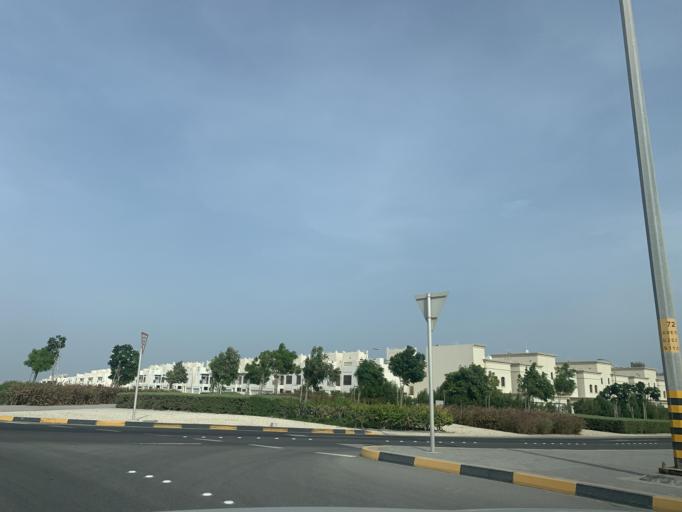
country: BH
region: Muharraq
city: Al Muharraq
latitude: 26.3186
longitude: 50.6250
